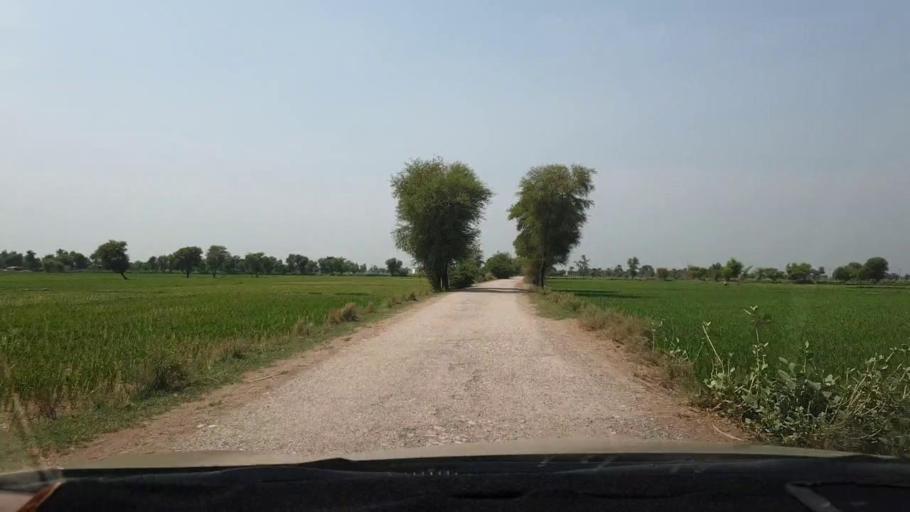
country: PK
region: Sindh
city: Naudero
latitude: 27.6438
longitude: 68.2748
